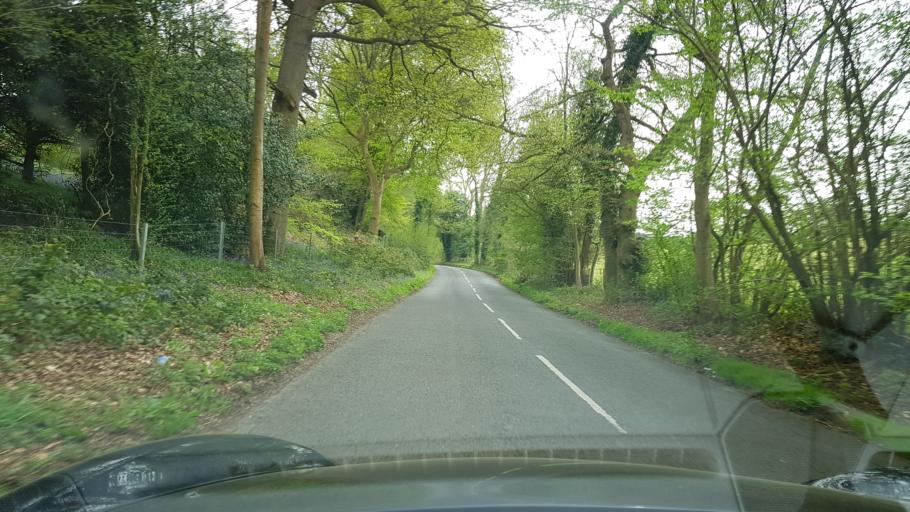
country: GB
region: England
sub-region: Surrey
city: East Horsley
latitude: 51.2448
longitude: -0.4416
